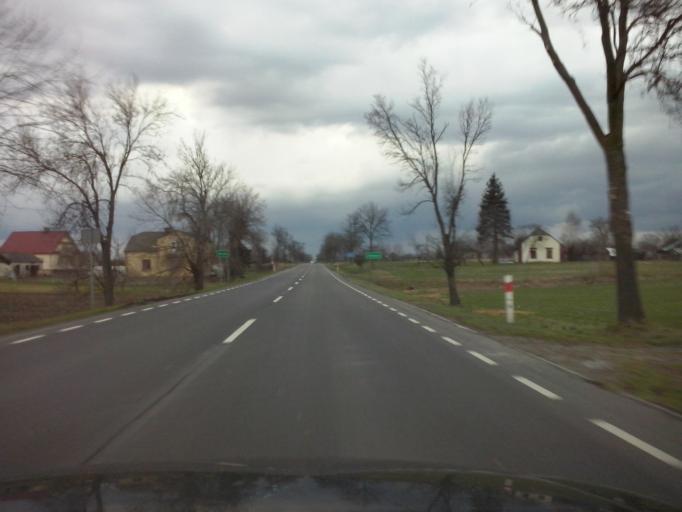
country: PL
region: Lublin Voivodeship
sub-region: Powiat chelmski
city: Rejowiec Fabryczny
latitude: 51.1711
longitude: 23.3082
